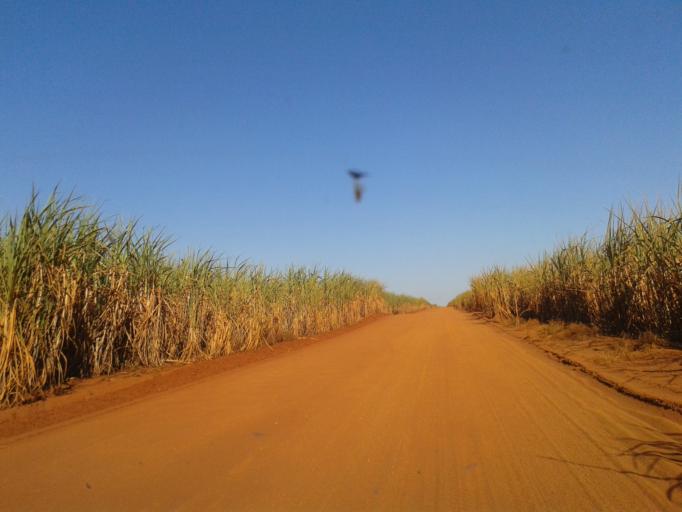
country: BR
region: Minas Gerais
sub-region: Santa Vitoria
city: Santa Vitoria
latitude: -18.8295
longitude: -50.0645
